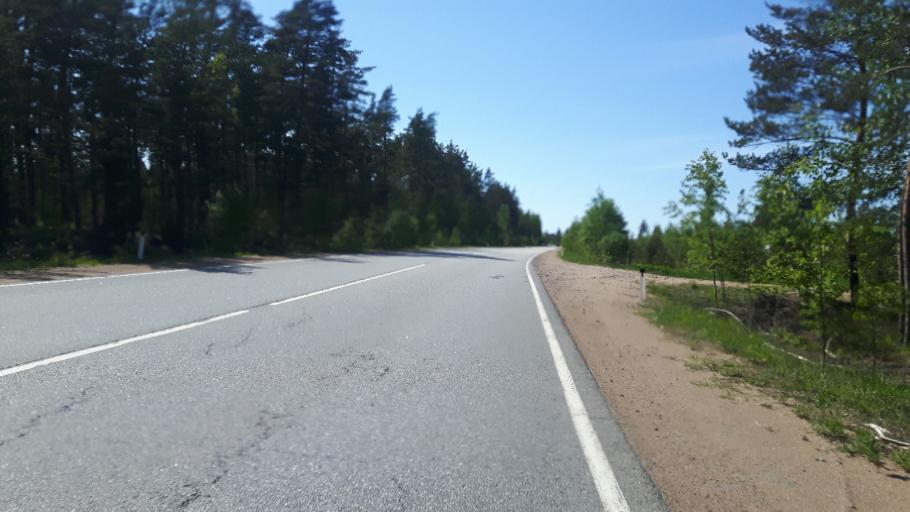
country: RU
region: Leningrad
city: Sista-Palkino
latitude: 59.7681
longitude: 28.7988
